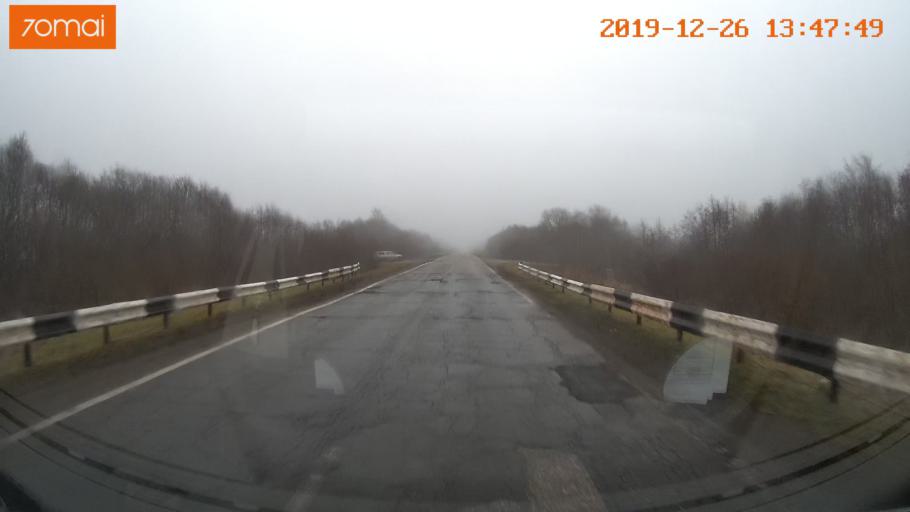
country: RU
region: Vologda
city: Sheksna
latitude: 58.6817
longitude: 38.5388
